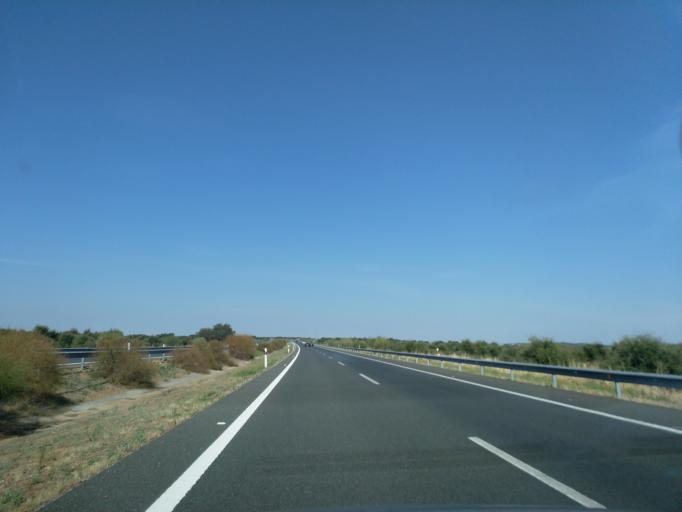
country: ES
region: Extremadura
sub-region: Provincia de Caceres
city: Casas de Don Antonio
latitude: 39.2579
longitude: -6.3124
